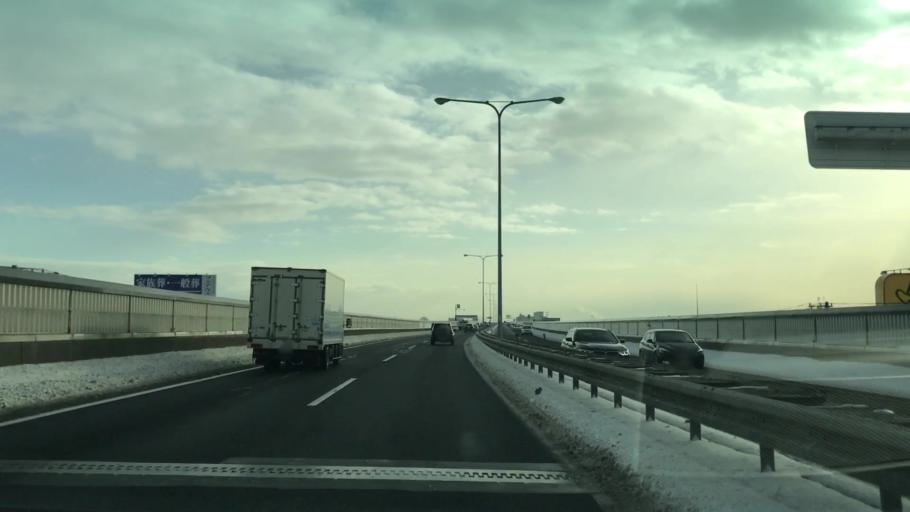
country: JP
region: Hokkaido
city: Sapporo
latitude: 43.1034
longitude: 141.3789
